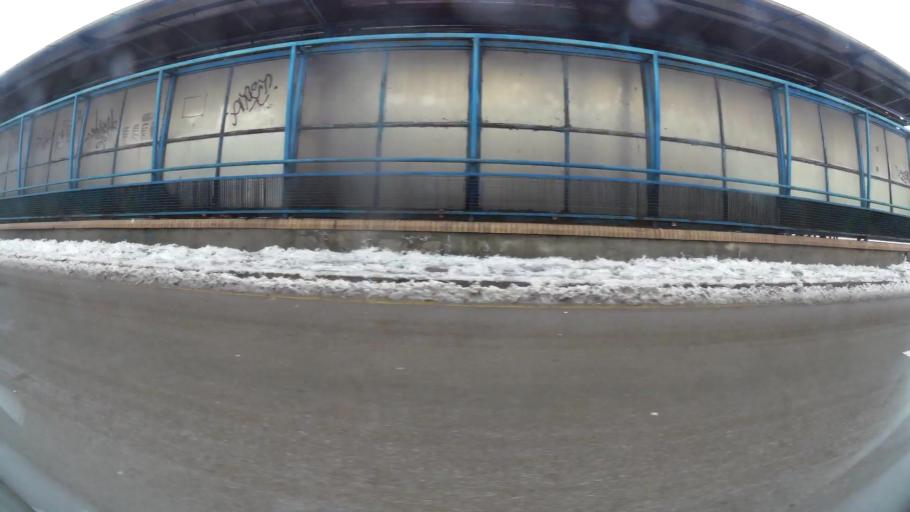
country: BG
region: Sofia-Capital
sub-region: Stolichna Obshtina
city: Sofia
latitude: 42.7113
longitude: 23.3199
